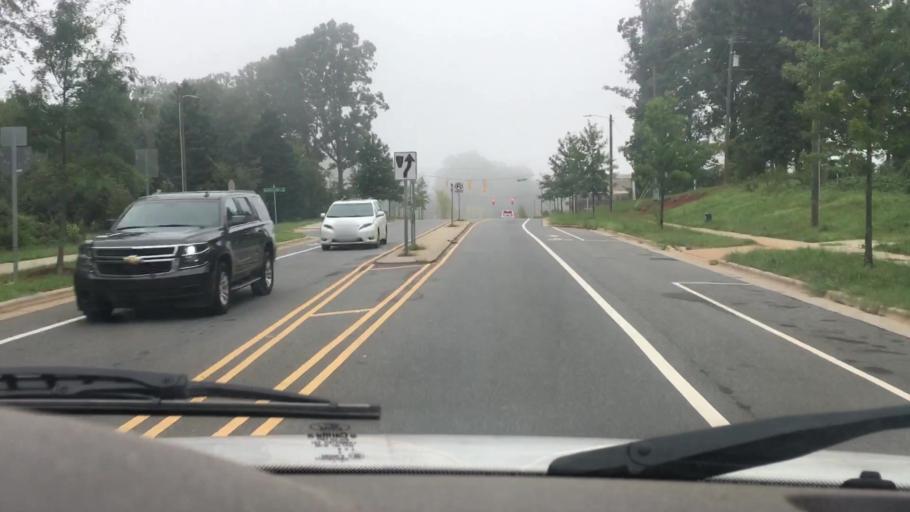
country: US
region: North Carolina
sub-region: Mecklenburg County
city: Huntersville
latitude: 35.3713
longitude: -80.7894
